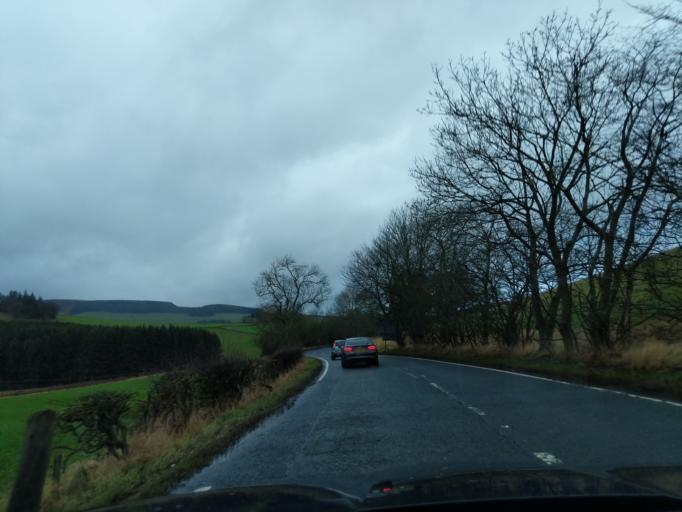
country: GB
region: Scotland
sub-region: The Scottish Borders
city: Galashiels
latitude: 55.6542
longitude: -2.8668
